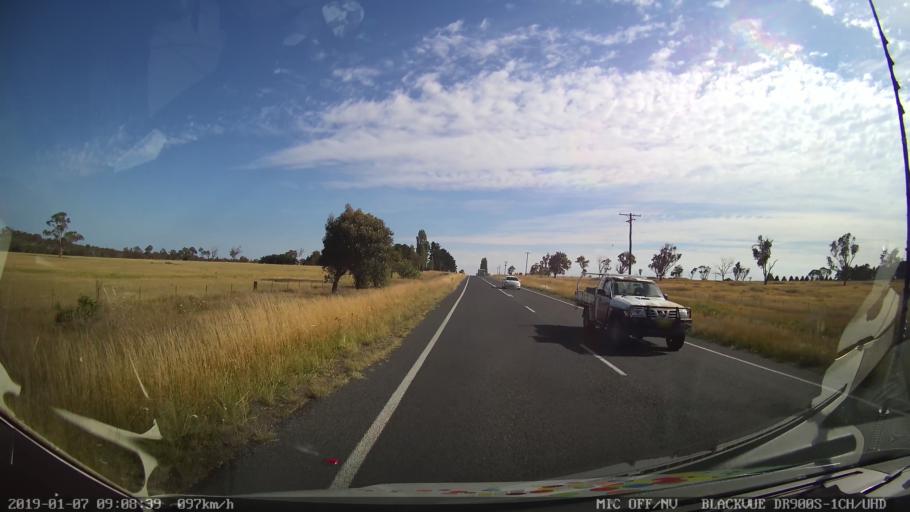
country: AU
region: New South Wales
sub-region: Armidale Dumaresq
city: Armidale
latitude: -30.6693
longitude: 151.4838
